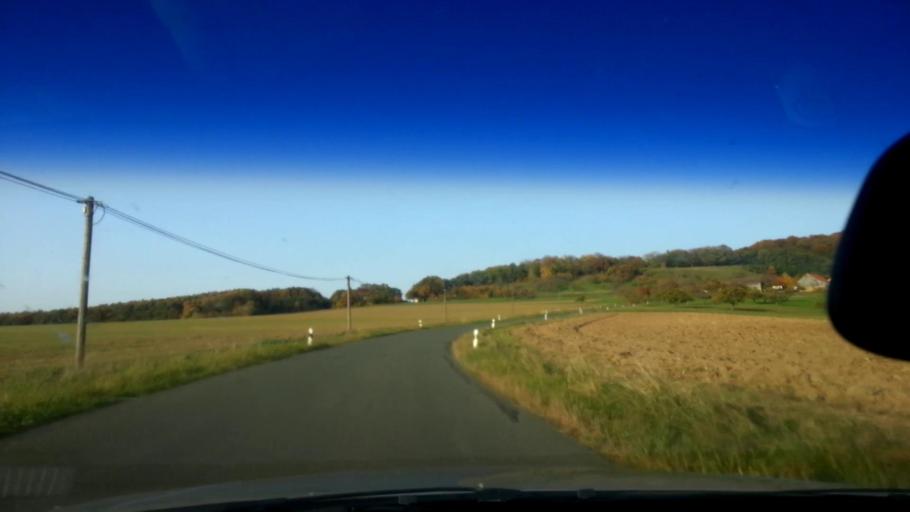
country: DE
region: Bavaria
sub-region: Upper Franconia
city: Schesslitz
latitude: 50.0141
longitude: 11.0199
